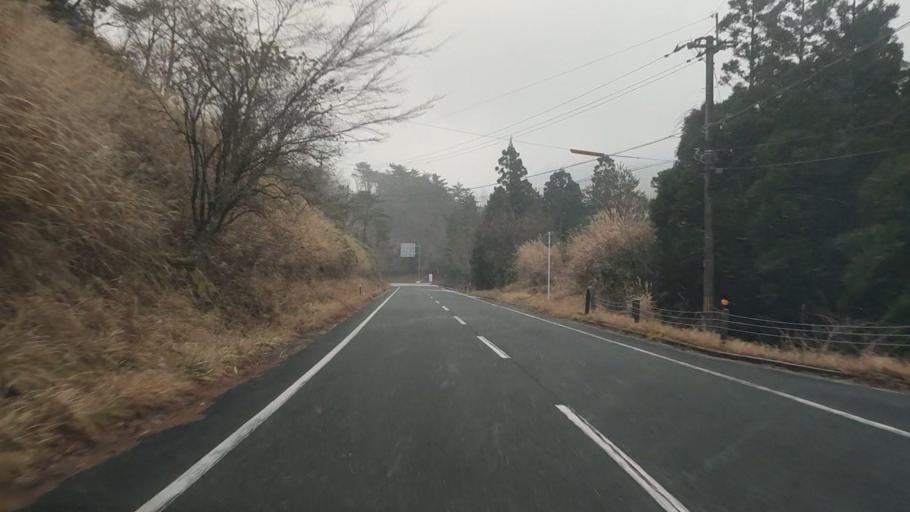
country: JP
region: Kumamoto
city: Matsubase
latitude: 32.5711
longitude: 130.9073
